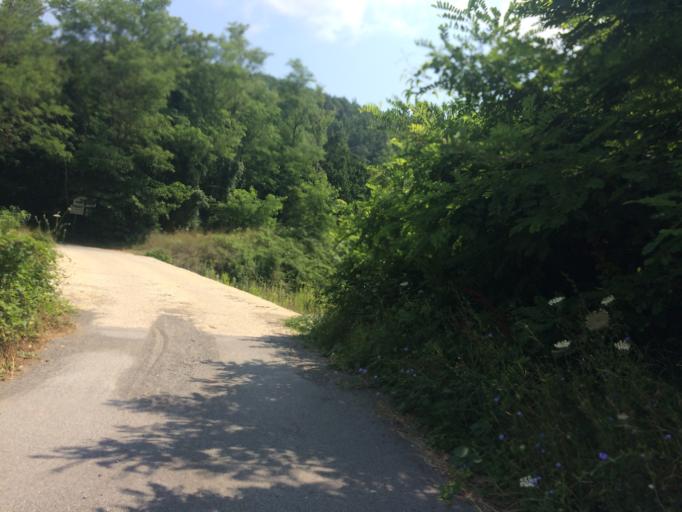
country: IT
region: Liguria
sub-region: Provincia di Savona
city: Molino-Pera
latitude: 44.4745
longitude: 8.3518
